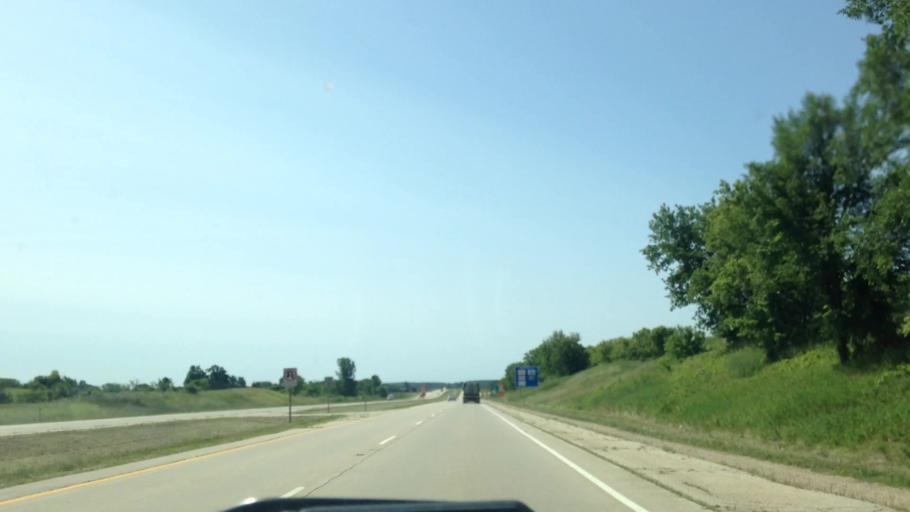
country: US
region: Wisconsin
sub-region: Washington County
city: Jackson
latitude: 43.3339
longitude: -88.1898
